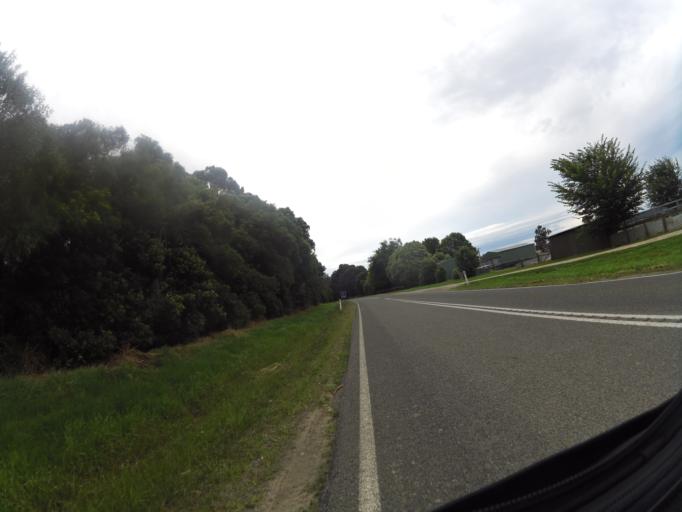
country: AU
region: Victoria
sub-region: East Gippsland
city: Lakes Entrance
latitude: -37.7214
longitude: 148.4921
